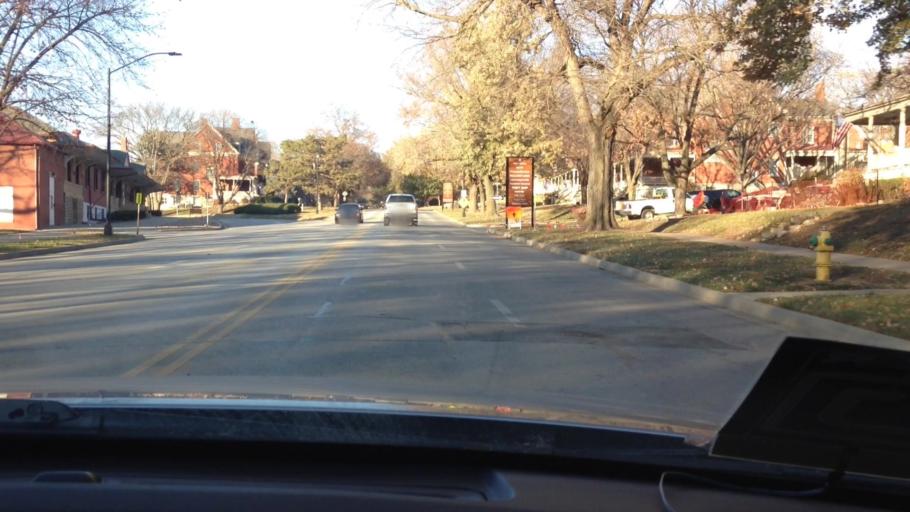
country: US
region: Kansas
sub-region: Leavenworth County
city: Leavenworth
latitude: 39.3511
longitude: -94.9183
